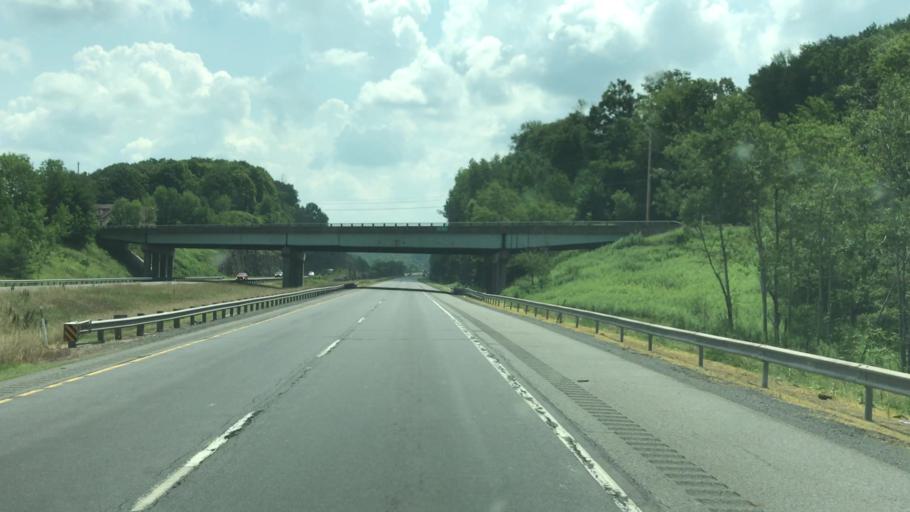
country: US
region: Pennsylvania
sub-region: Lackawanna County
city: Mount Cobb
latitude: 41.3972
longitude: -75.4821
